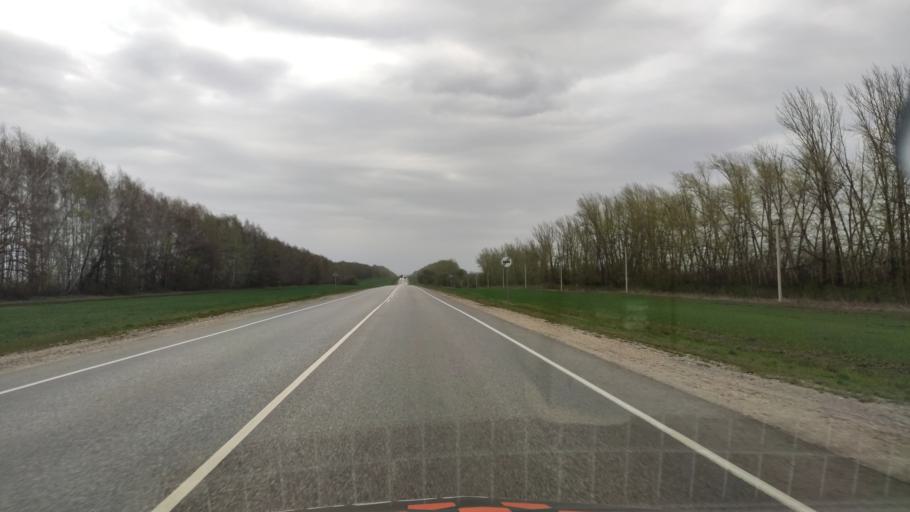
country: RU
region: Kursk
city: Gorshechnoye
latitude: 51.5491
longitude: 38.1425
